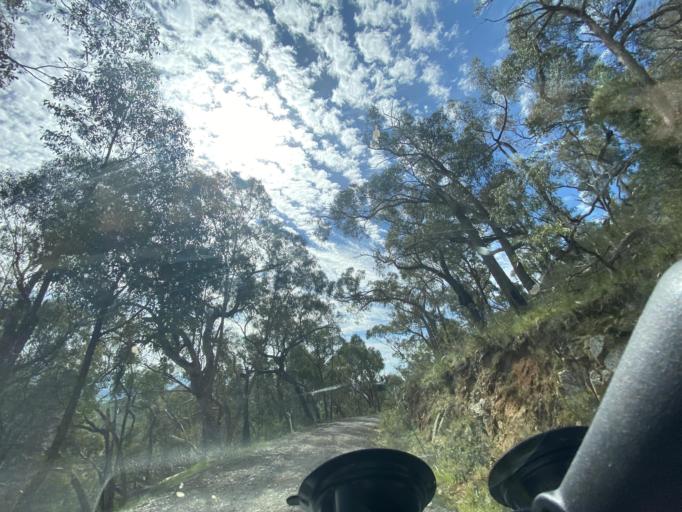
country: AU
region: Victoria
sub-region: Mansfield
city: Mansfield
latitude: -36.8094
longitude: 146.1030
